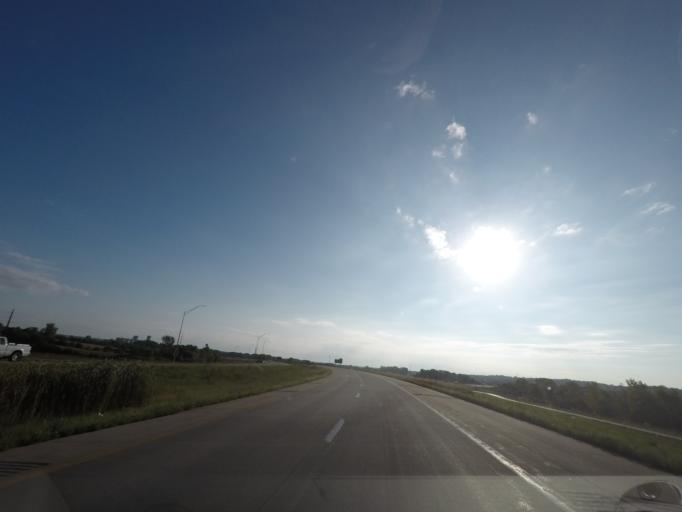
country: US
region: Iowa
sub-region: Warren County
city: Carlisle
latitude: 41.5111
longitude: -93.5278
